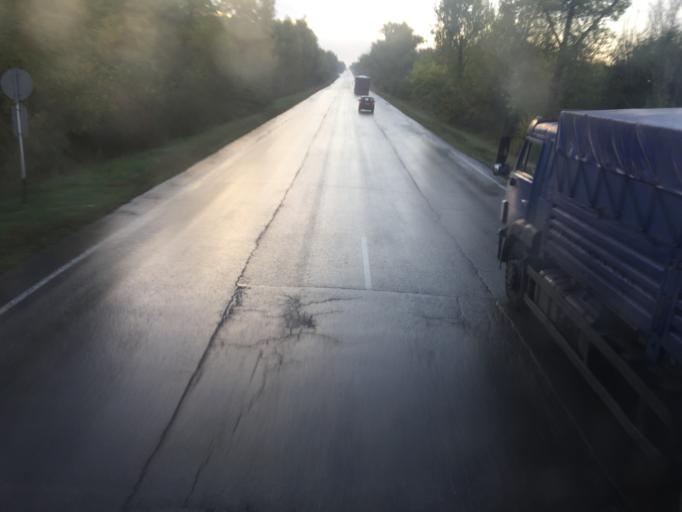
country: RU
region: Rostov
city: Bataysk
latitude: 47.0349
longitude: 39.8698
